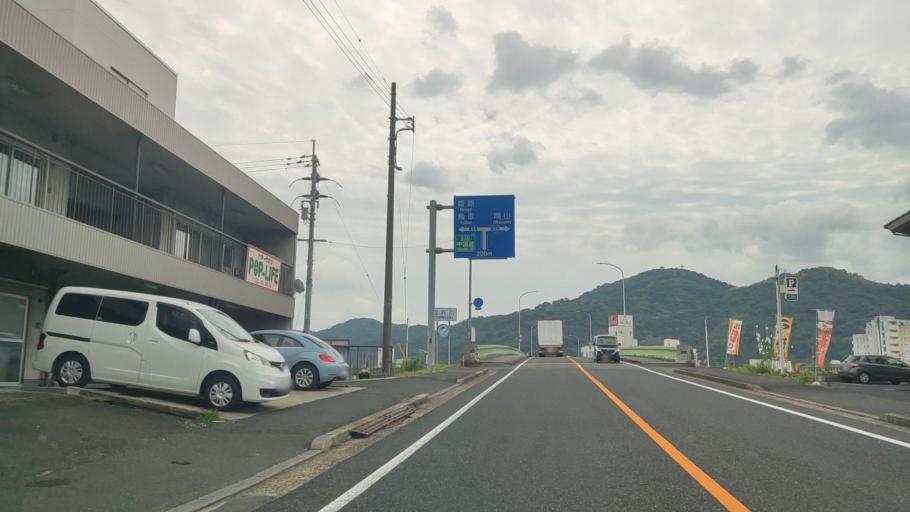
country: JP
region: Okayama
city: Tsuyama
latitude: 35.0600
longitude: 133.9793
